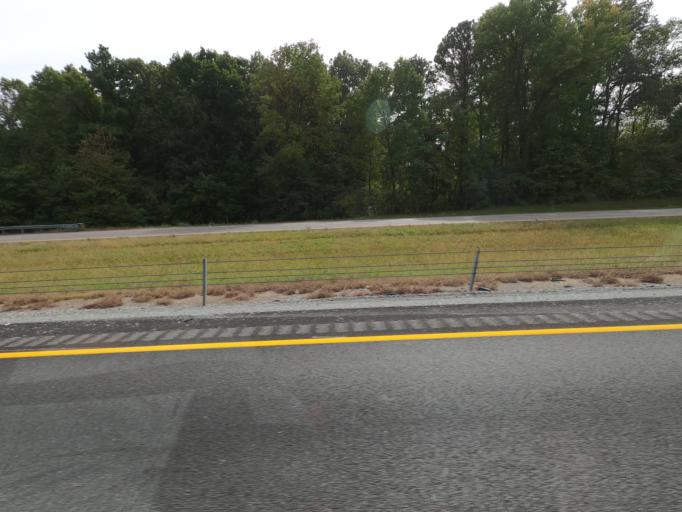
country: US
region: Tennessee
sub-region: Crockett County
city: Bells
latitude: 35.6213
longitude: -88.9876
